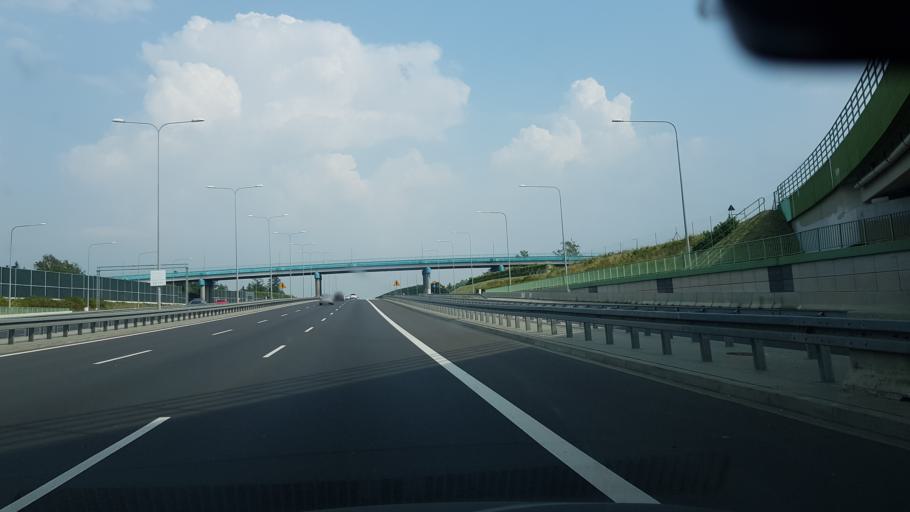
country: PL
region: Masovian Voivodeship
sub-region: Powiat piaseczynski
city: Mysiadlo
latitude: 52.1388
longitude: 20.9923
